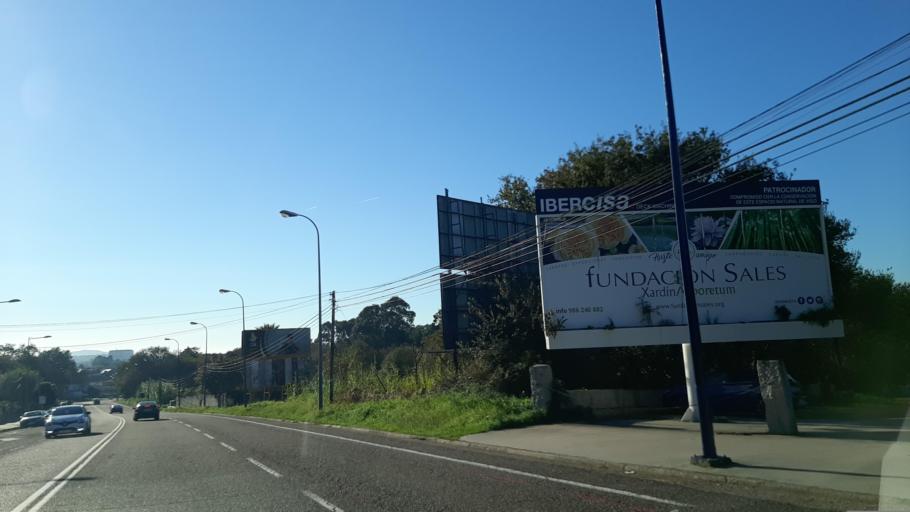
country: ES
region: Galicia
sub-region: Provincia de Pontevedra
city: Vigo
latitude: 42.2147
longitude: -8.7626
